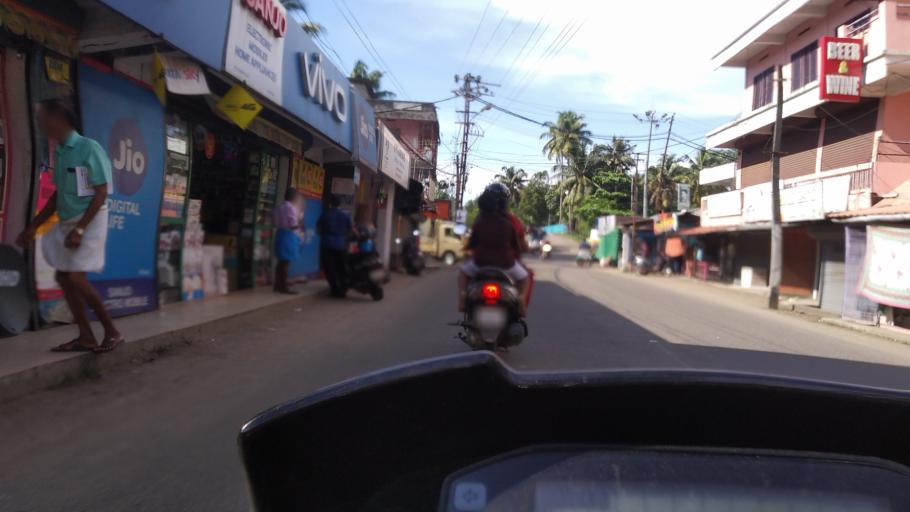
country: IN
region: Kerala
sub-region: Ernakulam
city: Elur
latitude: 10.0662
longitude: 76.2129
